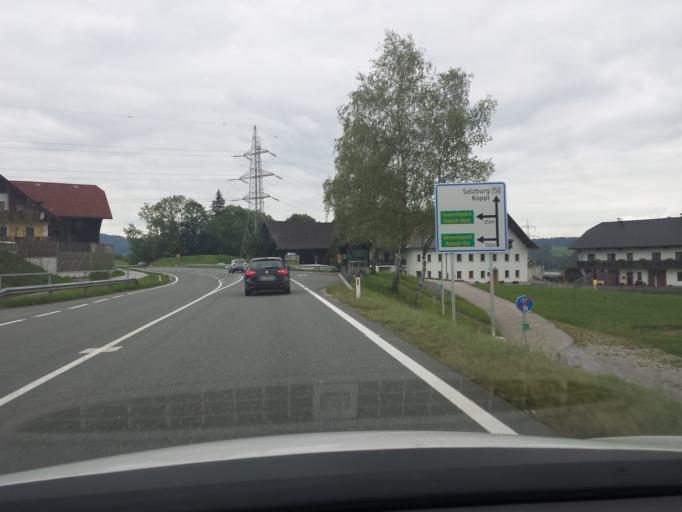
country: AT
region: Salzburg
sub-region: Politischer Bezirk Salzburg-Umgebung
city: Koppl
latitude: 47.8173
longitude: 13.1630
